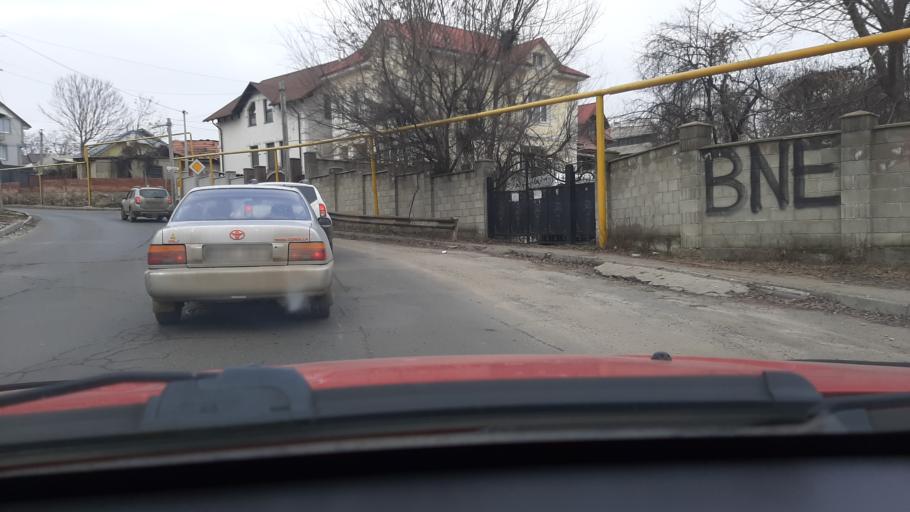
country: MD
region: Chisinau
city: Chisinau
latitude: 47.0078
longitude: 28.8403
